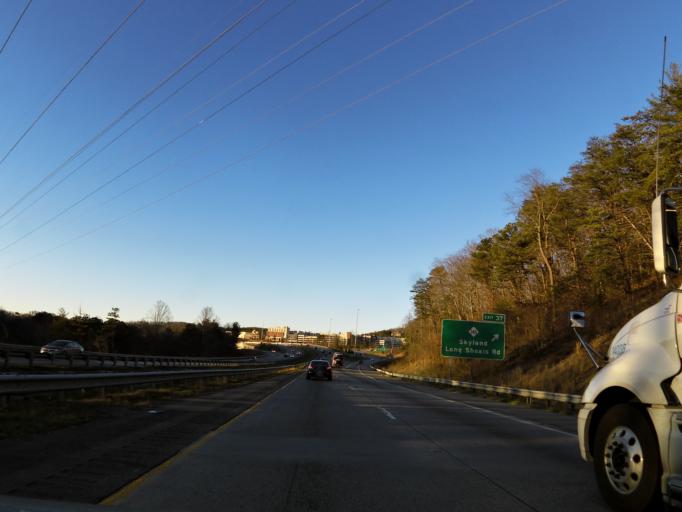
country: US
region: North Carolina
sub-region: Buncombe County
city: Avery Creek
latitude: 35.4771
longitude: -82.5544
